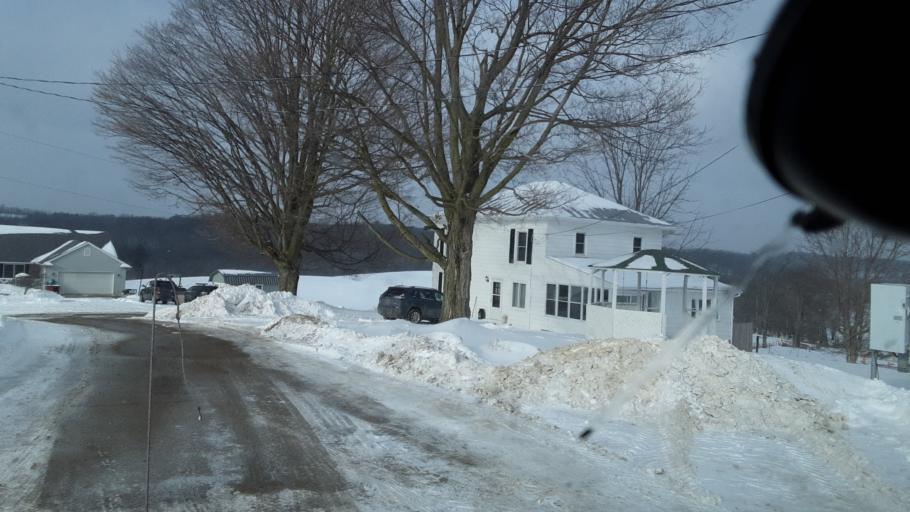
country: US
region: Ohio
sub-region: Sandusky County
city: Bellville
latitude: 40.6218
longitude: -82.4175
